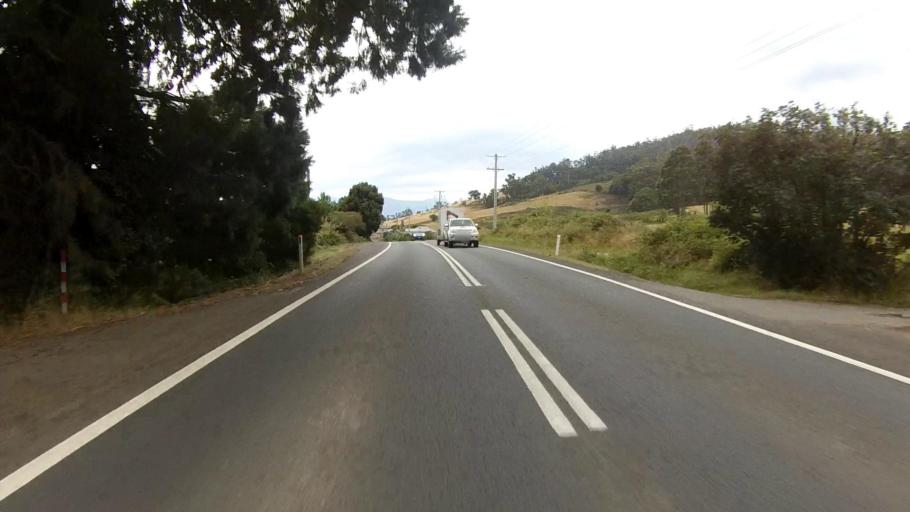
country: AU
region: Tasmania
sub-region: Huon Valley
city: Huonville
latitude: -43.0515
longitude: 147.0497
